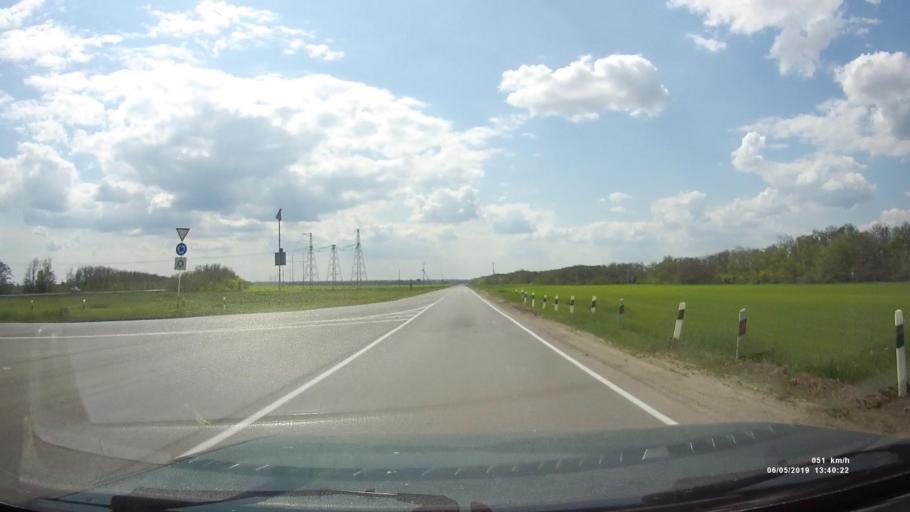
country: RU
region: Rostov
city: Ust'-Donetskiy
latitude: 47.6676
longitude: 40.6946
